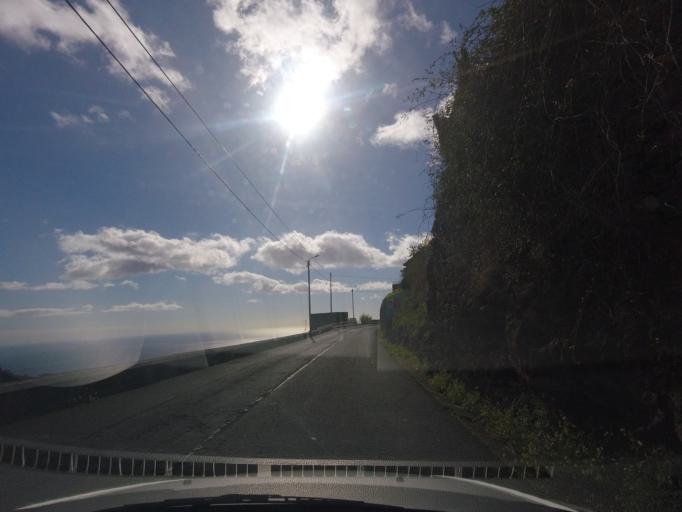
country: PT
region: Madeira
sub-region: Ribeira Brava
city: Campanario
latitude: 32.6610
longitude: -17.0143
